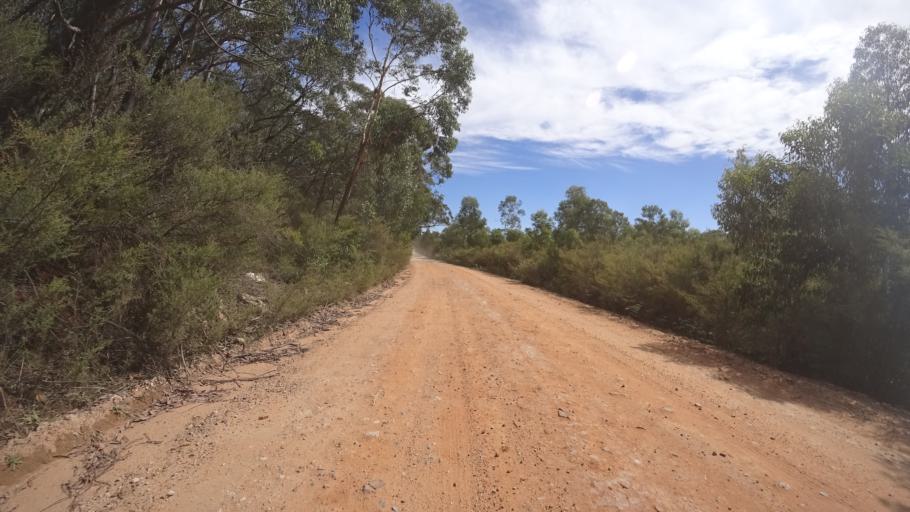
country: AU
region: New South Wales
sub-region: Lithgow
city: Lithgow
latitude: -33.3186
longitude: 150.2467
